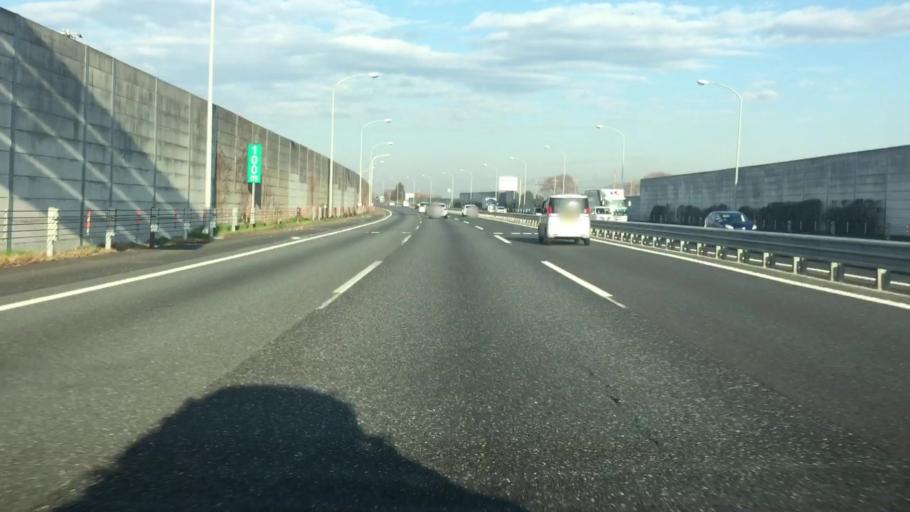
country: JP
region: Saitama
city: Kawagoe
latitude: 35.9052
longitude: 139.4511
